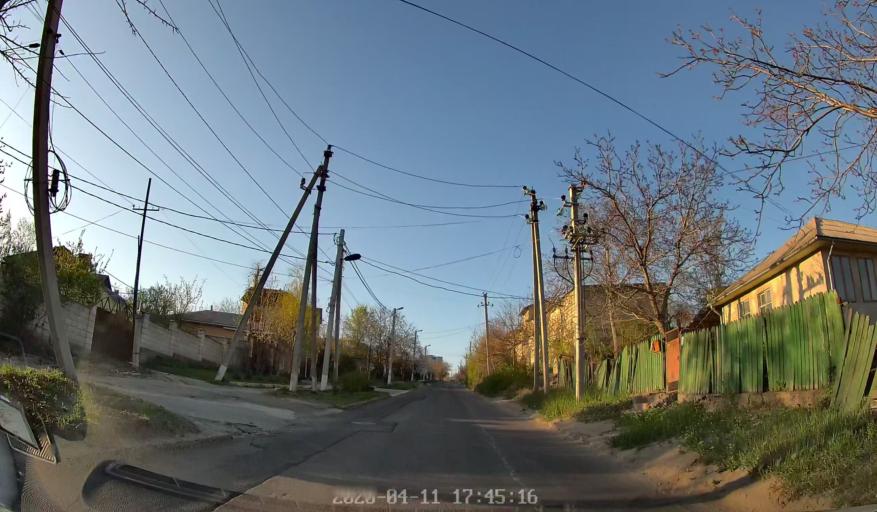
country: MD
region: Chisinau
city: Chisinau
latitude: 46.9836
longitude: 28.8228
